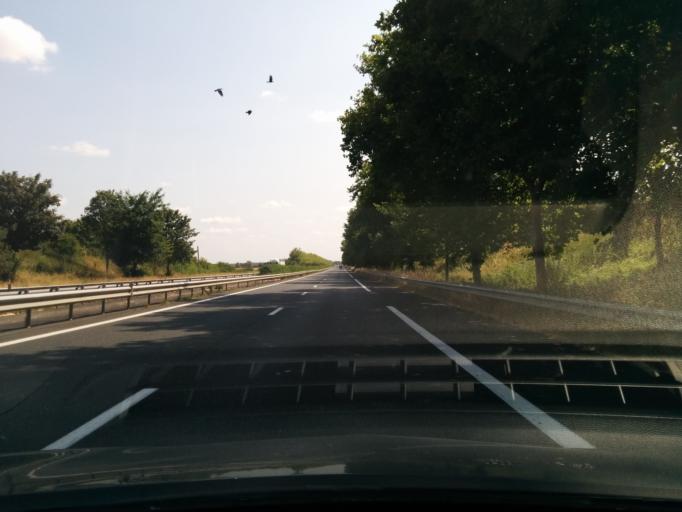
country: FR
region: Centre
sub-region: Departement de l'Indre
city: Montierchaume
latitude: 46.9037
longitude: 1.7344
